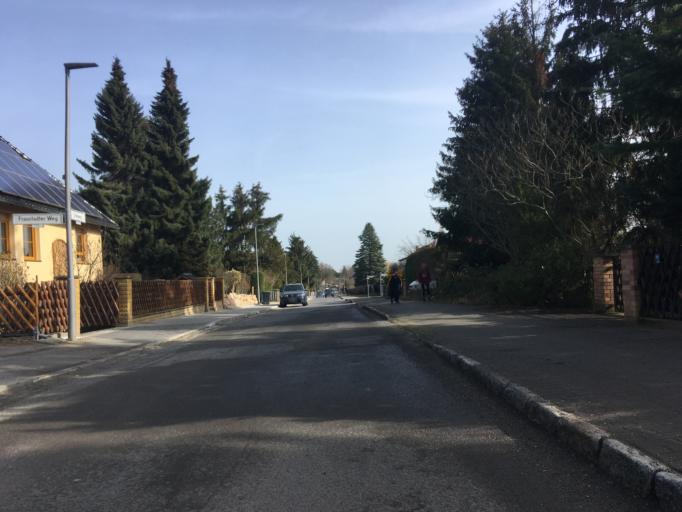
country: DE
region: Berlin
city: Bohnsdorf
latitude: 52.3984
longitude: 13.5697
